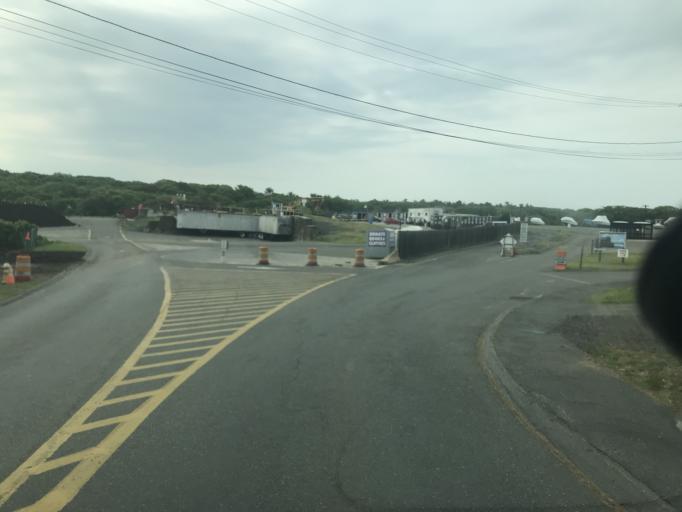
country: US
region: Massachusetts
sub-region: Essex County
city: Rockport
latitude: 42.6491
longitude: -70.6242
